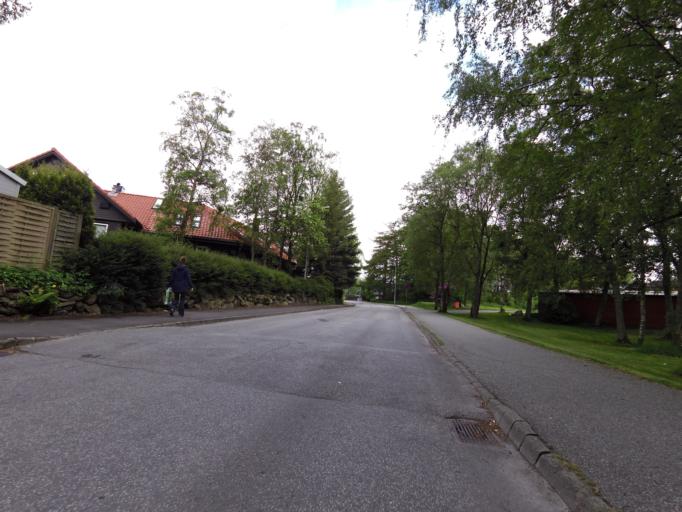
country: NO
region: Rogaland
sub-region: Stavanger
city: Stavanger
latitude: 58.9573
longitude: 5.6904
